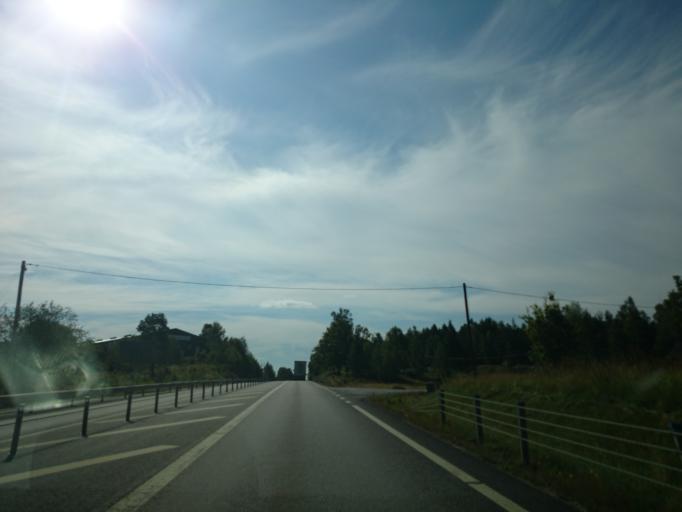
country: SE
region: Kalmar
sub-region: Vasterviks Kommun
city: Gamleby
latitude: 57.8700
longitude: 16.4115
